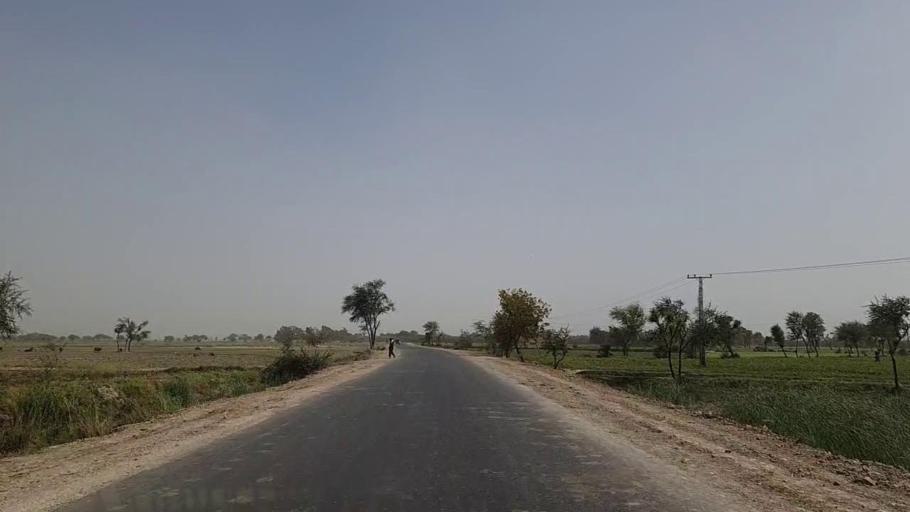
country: PK
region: Sindh
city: Tando Bago
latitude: 24.8134
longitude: 68.9109
